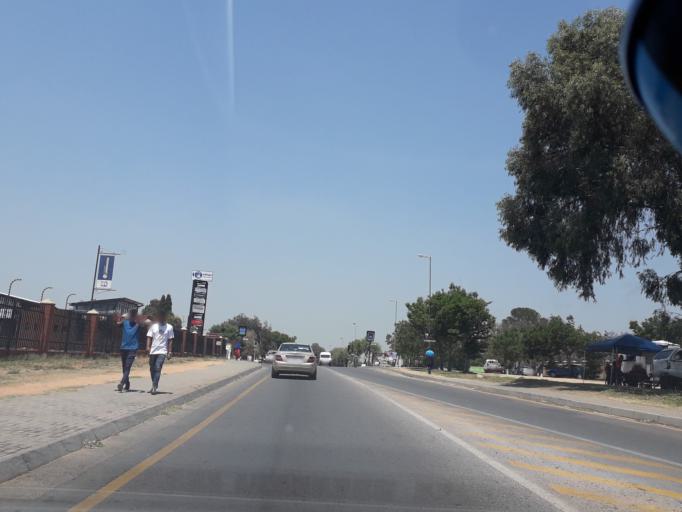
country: ZA
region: Gauteng
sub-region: City of Johannesburg Metropolitan Municipality
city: Midrand
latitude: -25.9813
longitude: 28.1177
